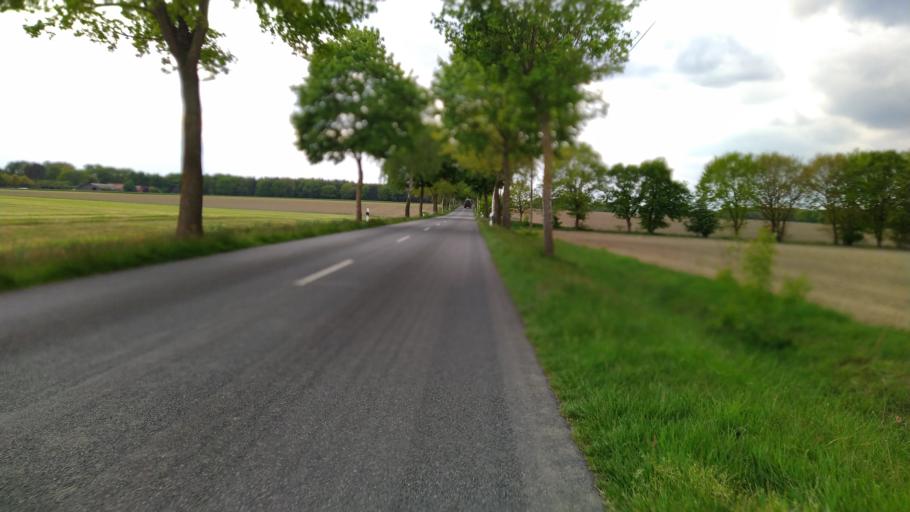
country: DE
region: Lower Saxony
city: Farven
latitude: 53.4302
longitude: 9.3134
